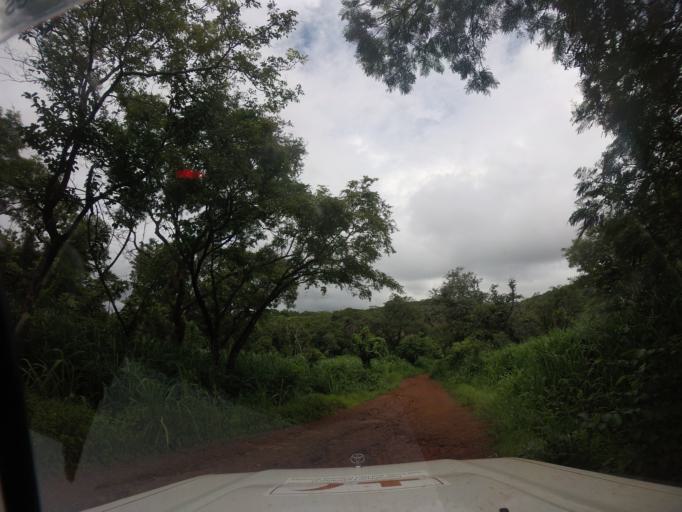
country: SL
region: Northern Province
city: Kamakwie
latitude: 9.6793
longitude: -12.2370
